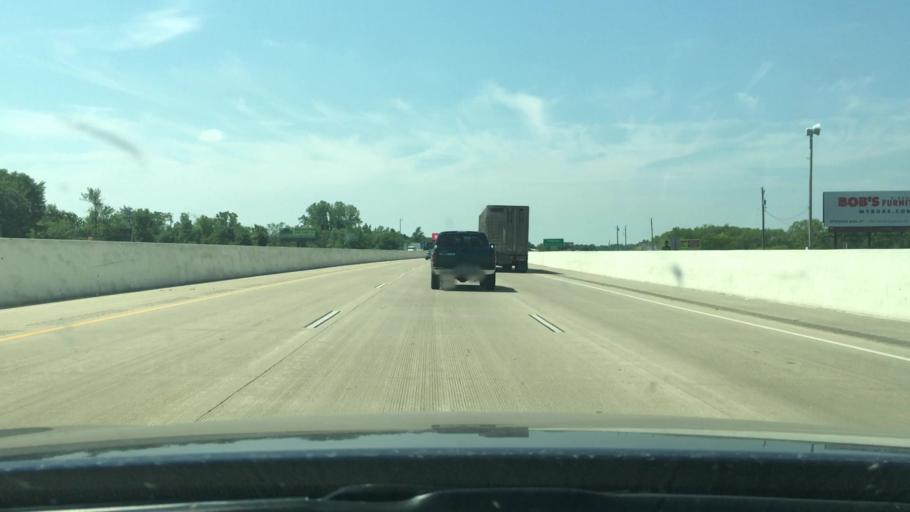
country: US
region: Wisconsin
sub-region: Winnebago County
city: Neenah
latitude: 44.1273
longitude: -88.4988
